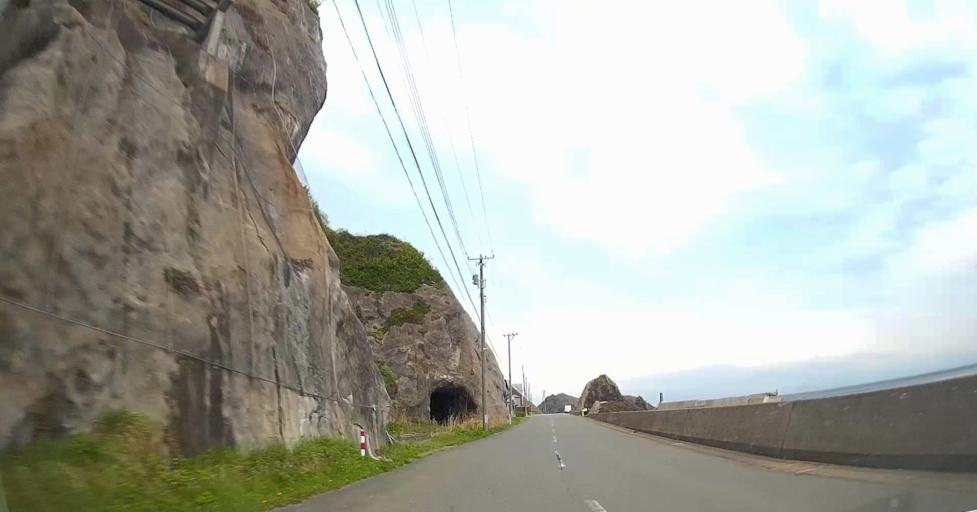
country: JP
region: Aomori
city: Shimokizukuri
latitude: 41.2564
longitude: 140.3508
